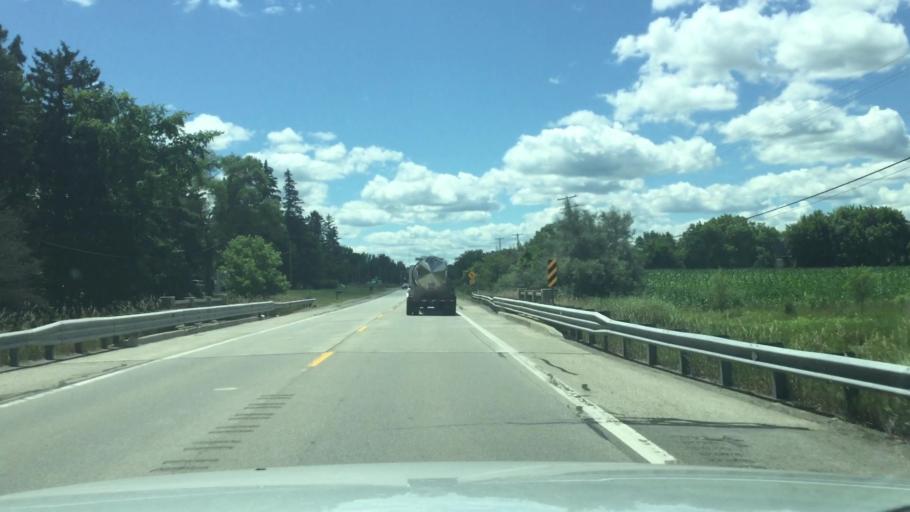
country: US
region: Michigan
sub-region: Saginaw County
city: Shields
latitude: 43.4080
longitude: -84.1309
